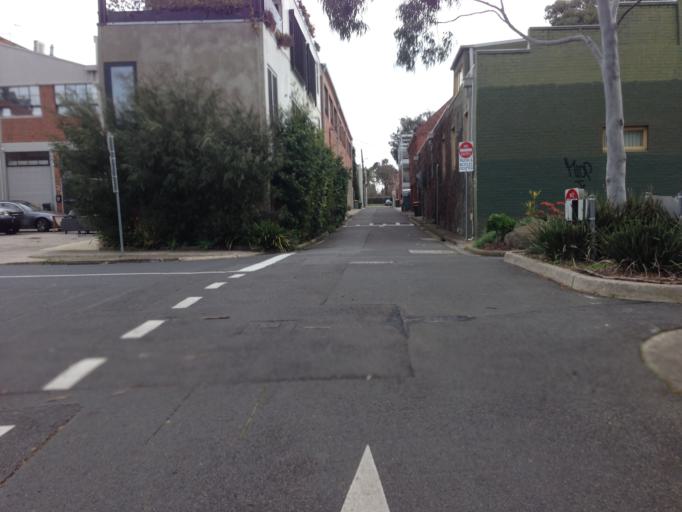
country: AU
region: Victoria
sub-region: Darebin
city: Fairfield
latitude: -37.7832
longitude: 145.0079
